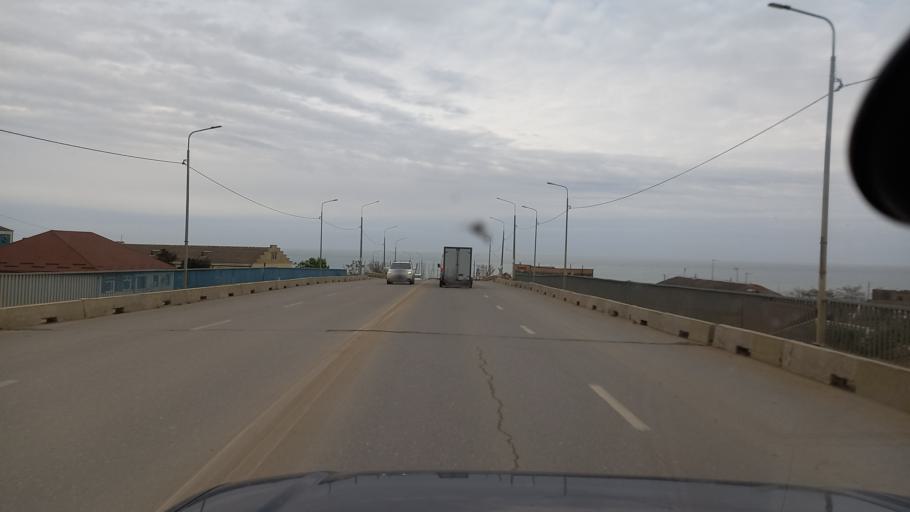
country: RU
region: Dagestan
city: Derbent
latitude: 42.0714
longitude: 48.2983
